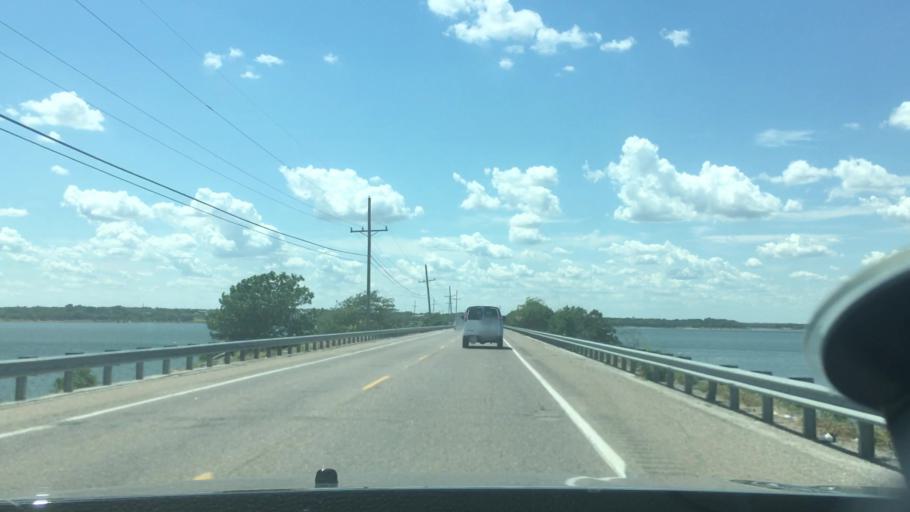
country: US
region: Oklahoma
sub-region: Marshall County
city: Kingston
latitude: 34.0016
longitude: -96.6113
